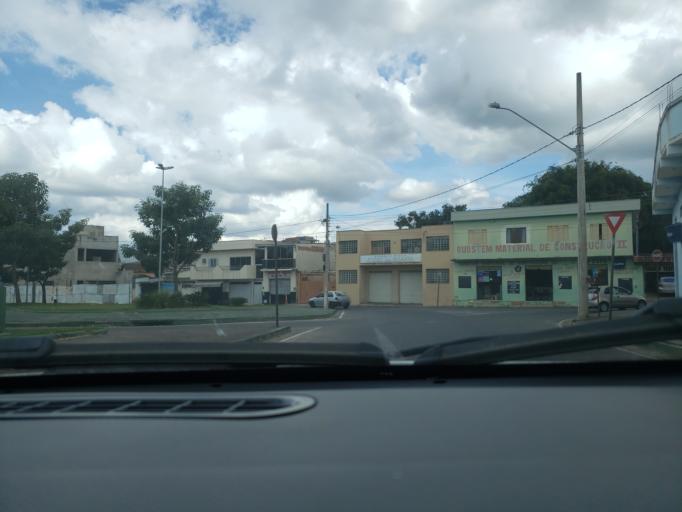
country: BR
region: Minas Gerais
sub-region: Campo Belo
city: Campo Belo
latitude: -20.9017
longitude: -45.2699
